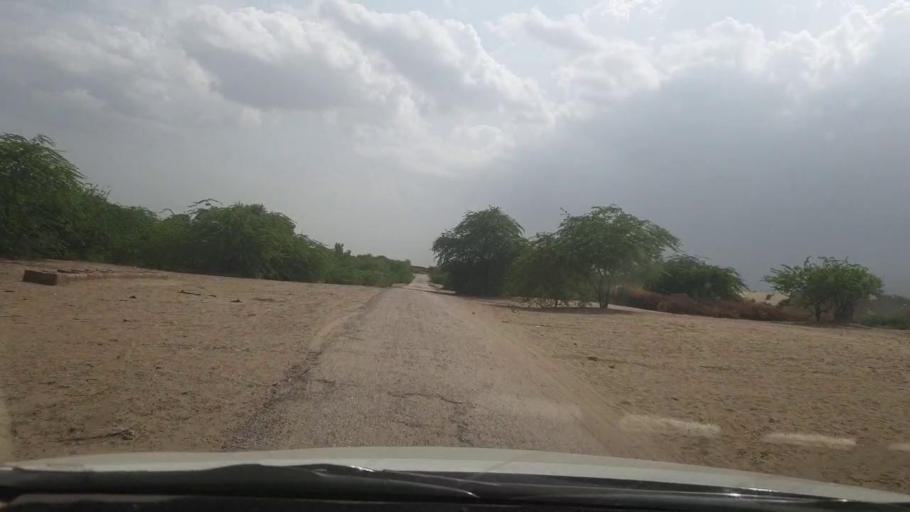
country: PK
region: Sindh
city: Kot Diji
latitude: 27.3424
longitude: 69.0200
